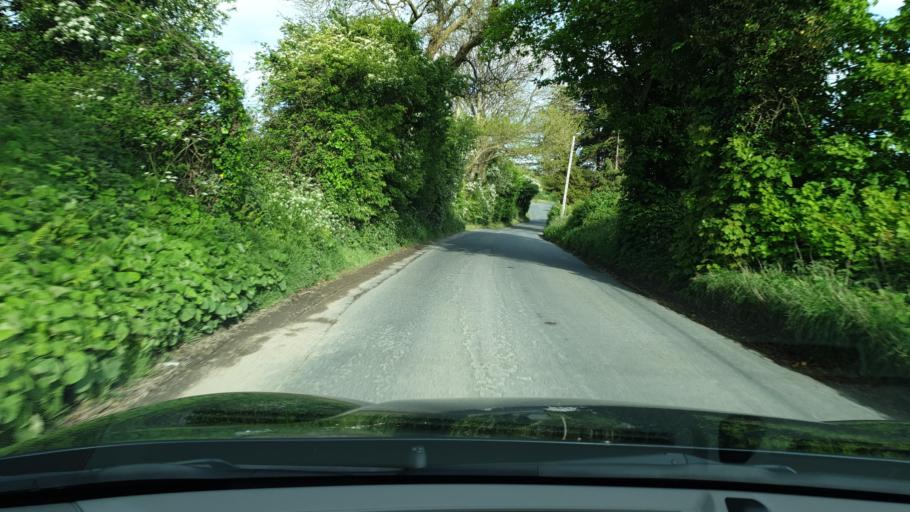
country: IE
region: Leinster
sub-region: An Mhi
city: Stamullin
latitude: 53.5576
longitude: -6.2620
